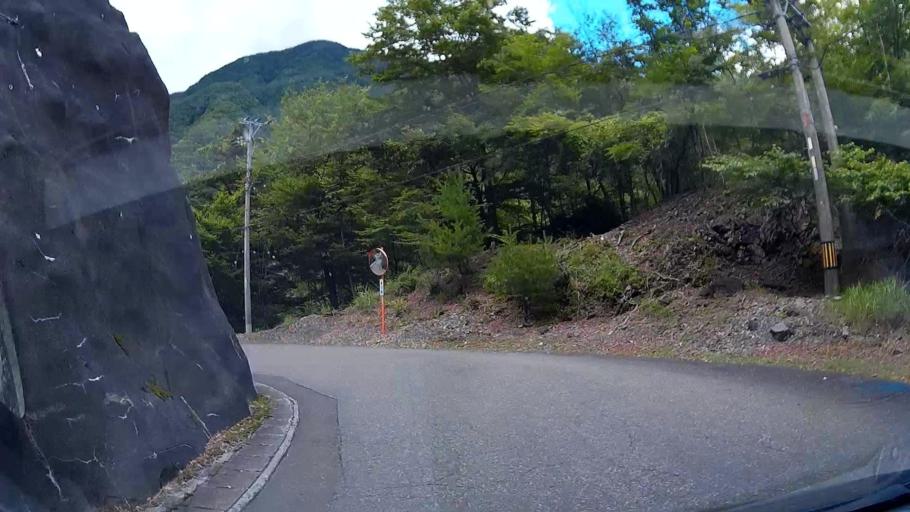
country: JP
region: Shizuoka
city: Shizuoka-shi
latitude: 35.3052
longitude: 138.2041
